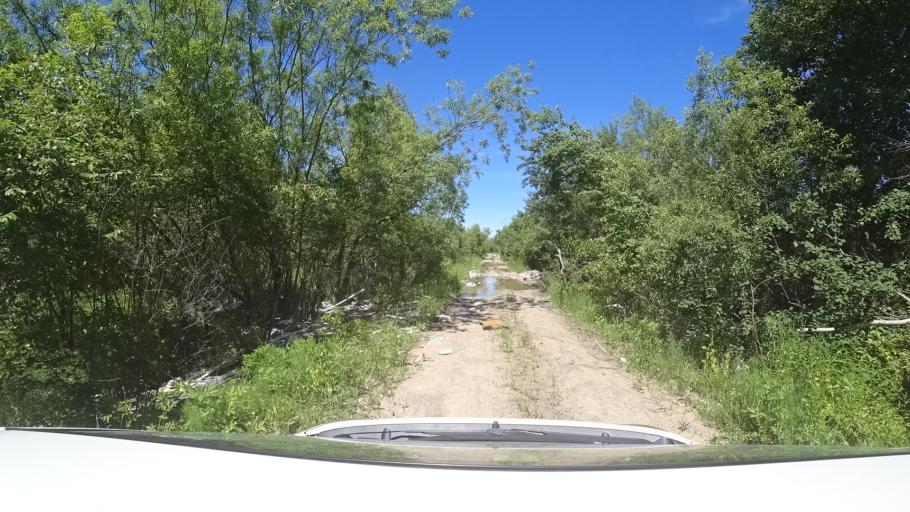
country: RU
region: Khabarovsk Krai
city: Topolevo
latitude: 48.4868
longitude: 135.1768
